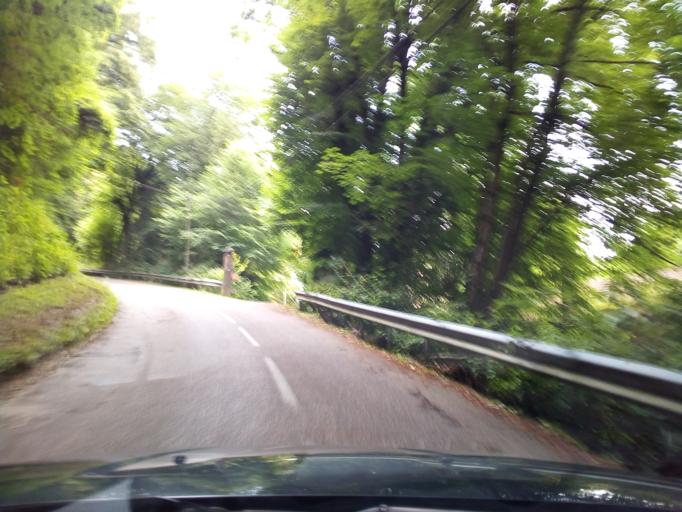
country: FR
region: Rhone-Alpes
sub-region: Departement de l'Isere
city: Gieres
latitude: 45.1768
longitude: 5.7795
